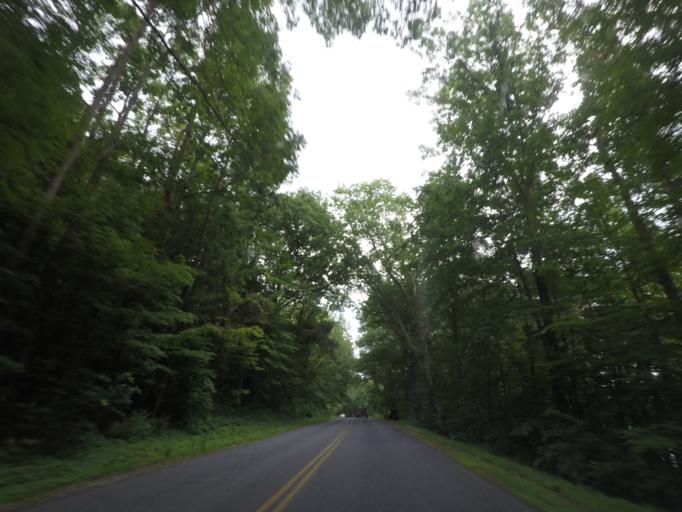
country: US
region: New York
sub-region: Saratoga County
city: Stillwater
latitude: 42.8414
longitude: -73.5335
